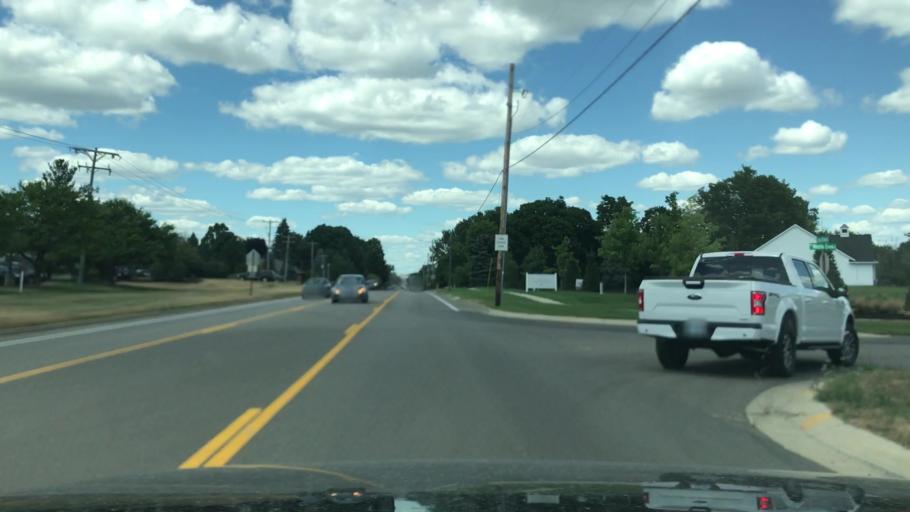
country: US
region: Michigan
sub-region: Kent County
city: Byron Center
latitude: 42.8205
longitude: -85.7230
